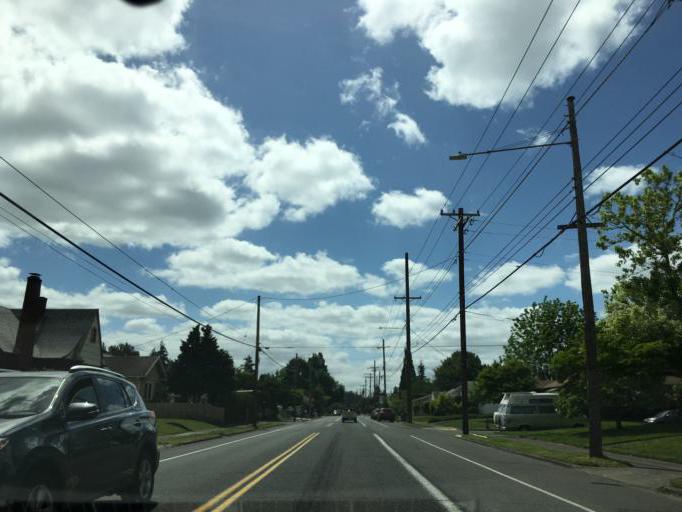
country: US
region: Oregon
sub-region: Multnomah County
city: Lents
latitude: 45.4861
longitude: -122.6088
